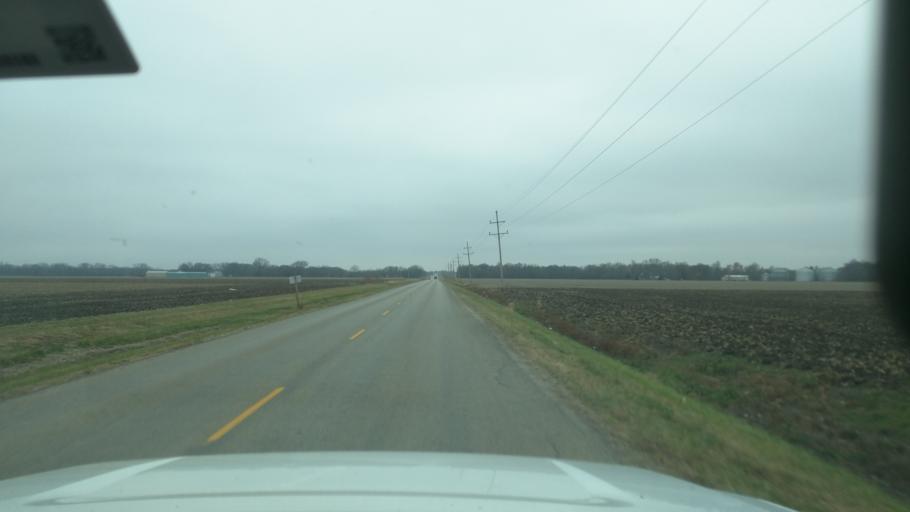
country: US
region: Kansas
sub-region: Lyon County
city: Emporia
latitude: 38.4795
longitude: -96.2530
